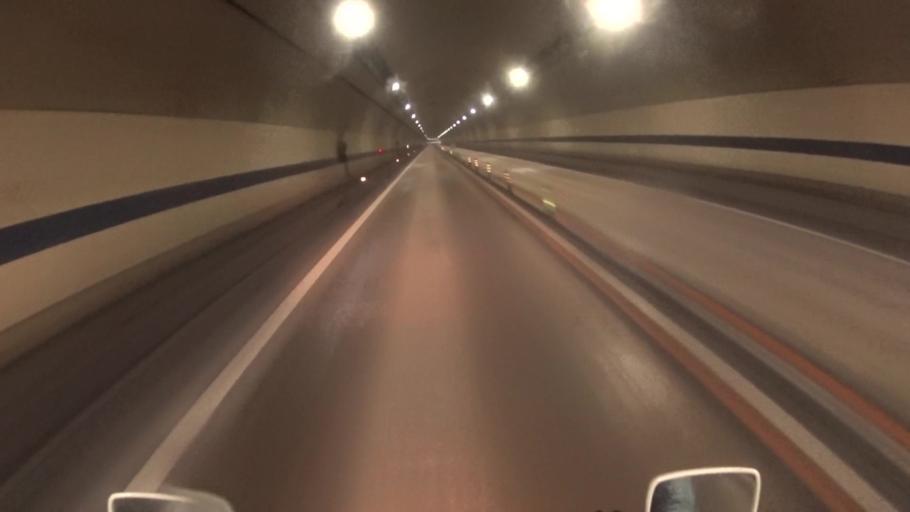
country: JP
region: Kyoto
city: Maizuru
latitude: 35.4154
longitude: 135.2194
